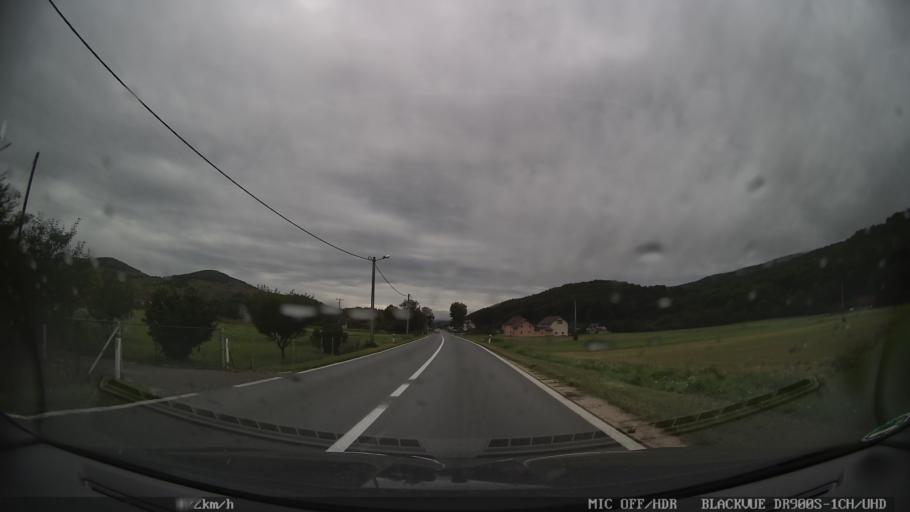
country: HR
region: Licko-Senjska
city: Brinje
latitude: 44.9377
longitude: 15.1271
